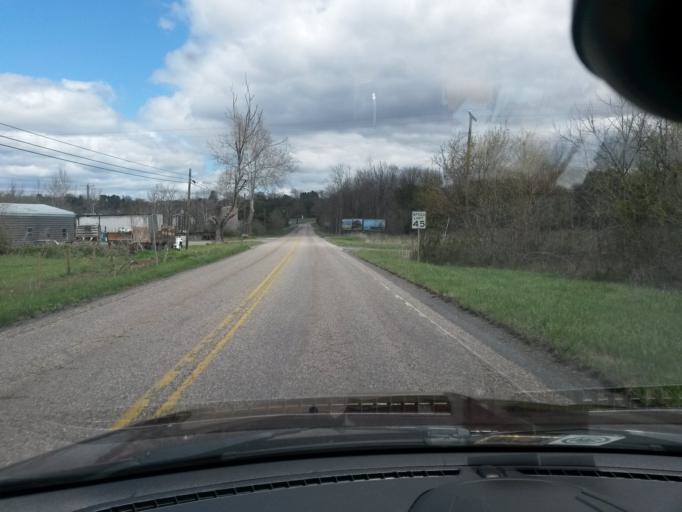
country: US
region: Virginia
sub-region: City of Buena Vista
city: Buena Vista
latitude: 37.7082
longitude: -79.3746
